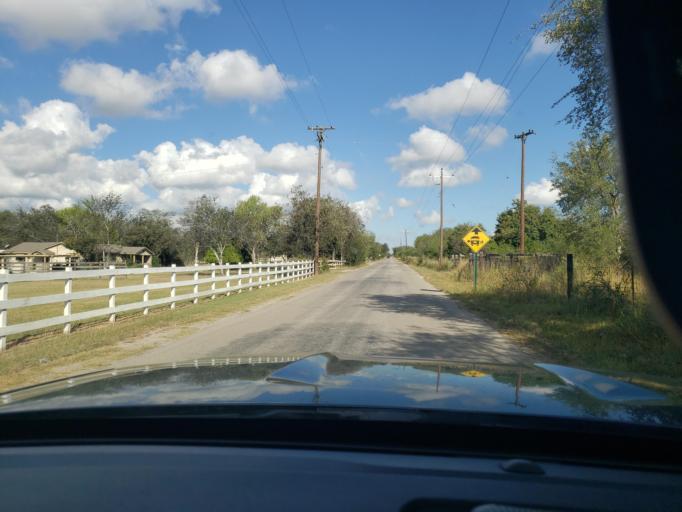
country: US
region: Texas
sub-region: Bee County
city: Beeville
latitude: 28.4404
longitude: -97.7128
